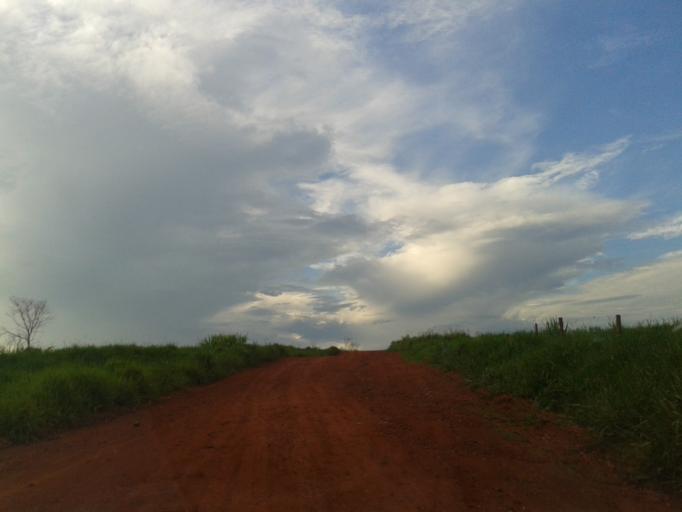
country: BR
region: Minas Gerais
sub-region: Santa Vitoria
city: Santa Vitoria
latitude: -19.0573
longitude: -50.4802
